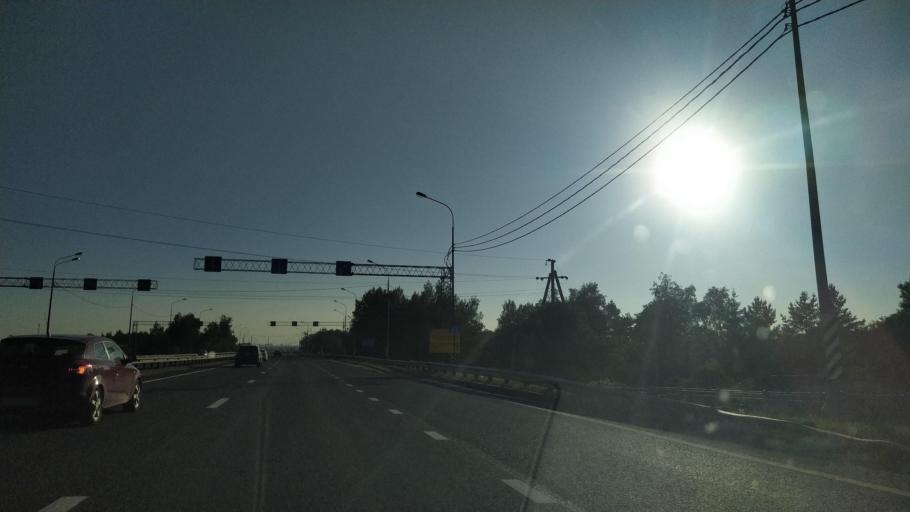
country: RU
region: Leningrad
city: Koltushi
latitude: 59.8979
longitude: 30.6867
